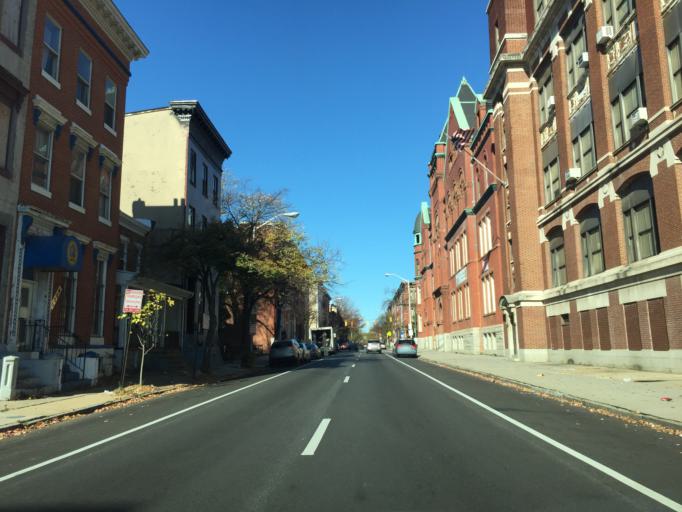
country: US
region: Maryland
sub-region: City of Baltimore
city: Baltimore
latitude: 39.3027
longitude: -76.6279
